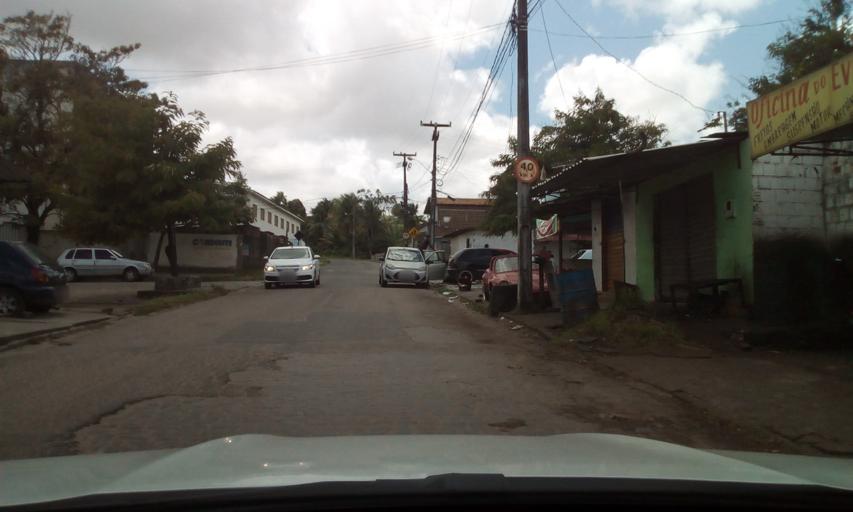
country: BR
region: Paraiba
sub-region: Joao Pessoa
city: Joao Pessoa
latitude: -7.1299
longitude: -34.8876
